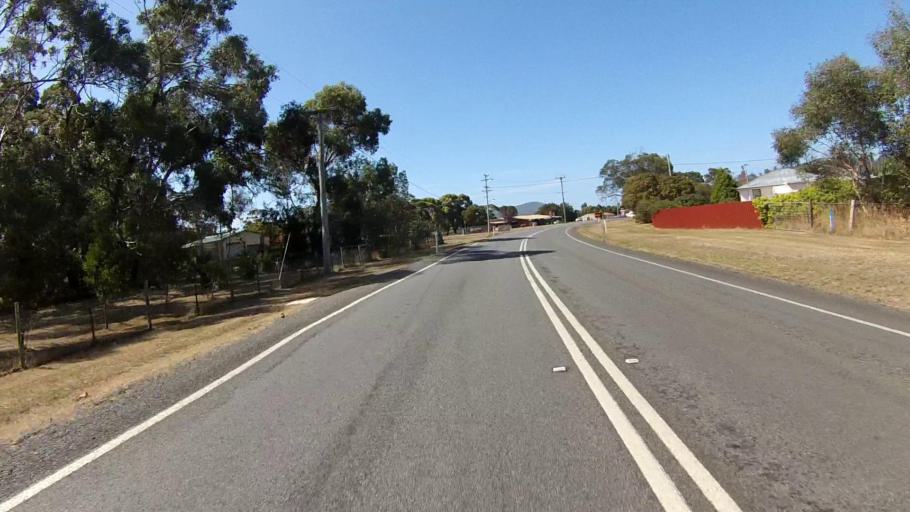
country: AU
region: Tasmania
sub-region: Sorell
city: Sorell
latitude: -42.5028
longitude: 147.9094
